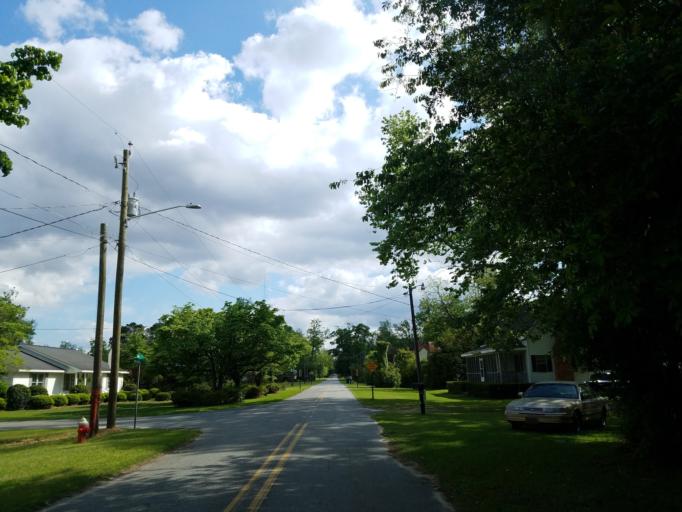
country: US
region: Georgia
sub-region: Dooly County
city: Unadilla
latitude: 32.1975
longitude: -83.7640
